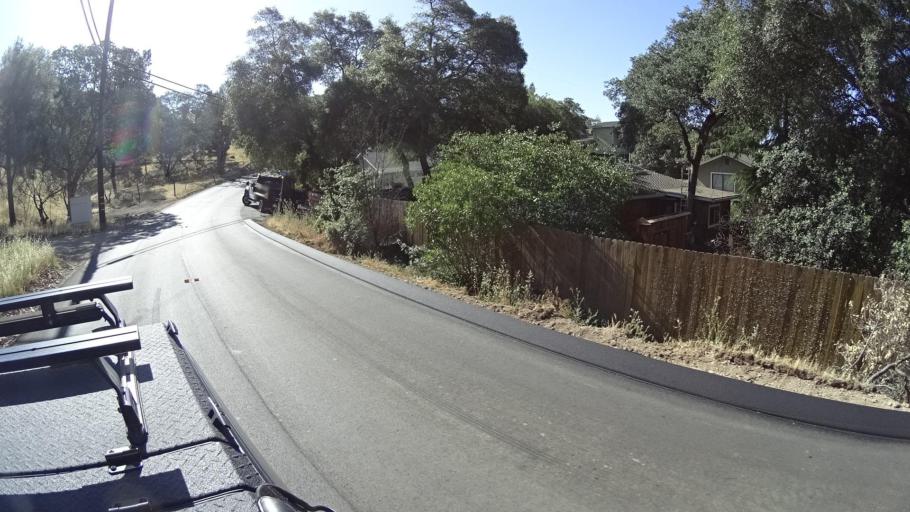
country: US
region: California
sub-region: Lake County
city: Clearlake Oaks
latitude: 38.9820
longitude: -122.6889
